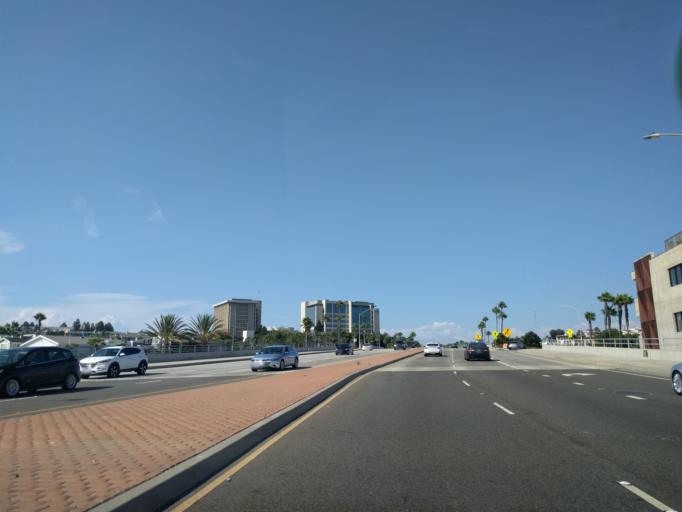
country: US
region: California
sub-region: Orange County
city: Newport Beach
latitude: 33.6195
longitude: -117.9299
